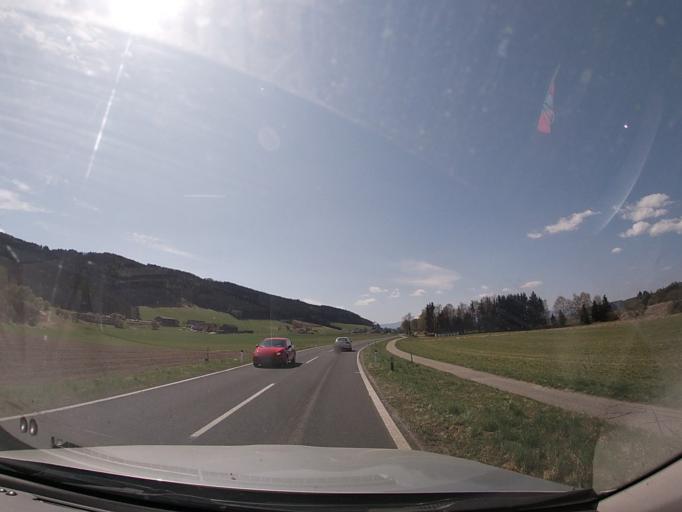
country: AT
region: Styria
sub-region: Politischer Bezirk Murtal
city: Sankt Lorenzen bei Knittelfeld
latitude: 47.2391
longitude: 14.8748
